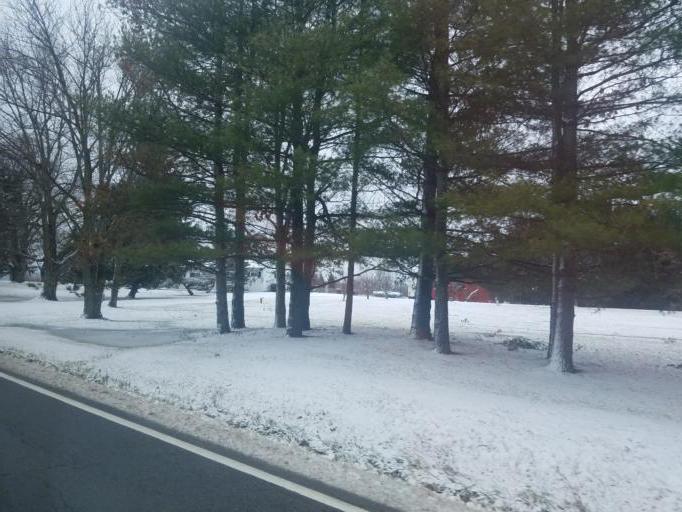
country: US
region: Ohio
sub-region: Licking County
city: Johnstown
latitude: 40.0959
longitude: -82.7122
